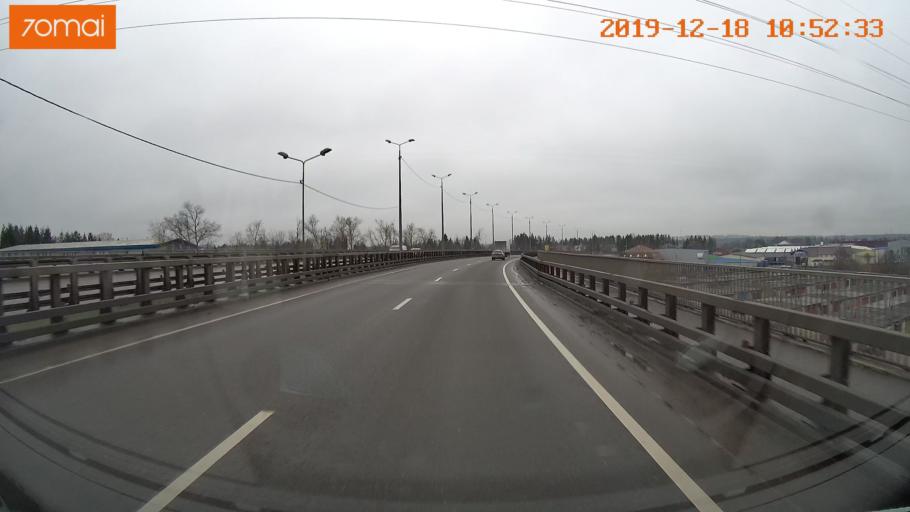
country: RU
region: Moskovskaya
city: Selyatino
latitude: 55.5259
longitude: 36.9801
